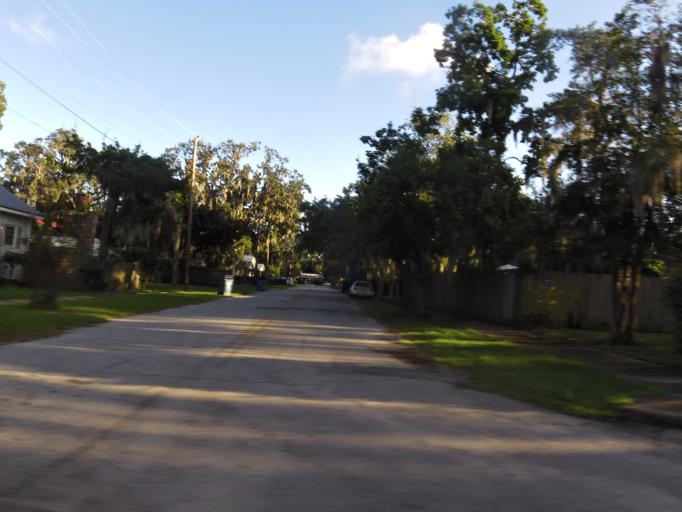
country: US
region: Georgia
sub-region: Glynn County
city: Brunswick
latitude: 31.1550
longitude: -81.4833
